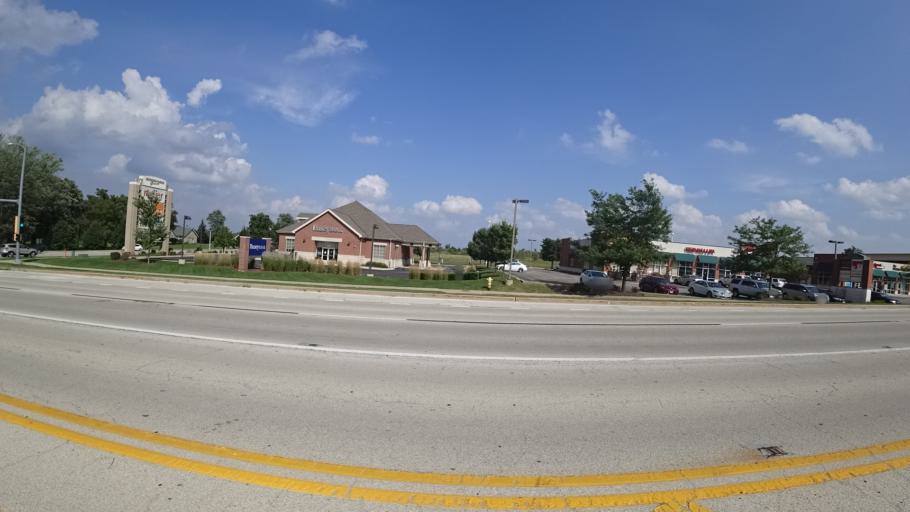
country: US
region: Illinois
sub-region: Will County
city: Goodings Grove
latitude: 41.6358
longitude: -87.9313
